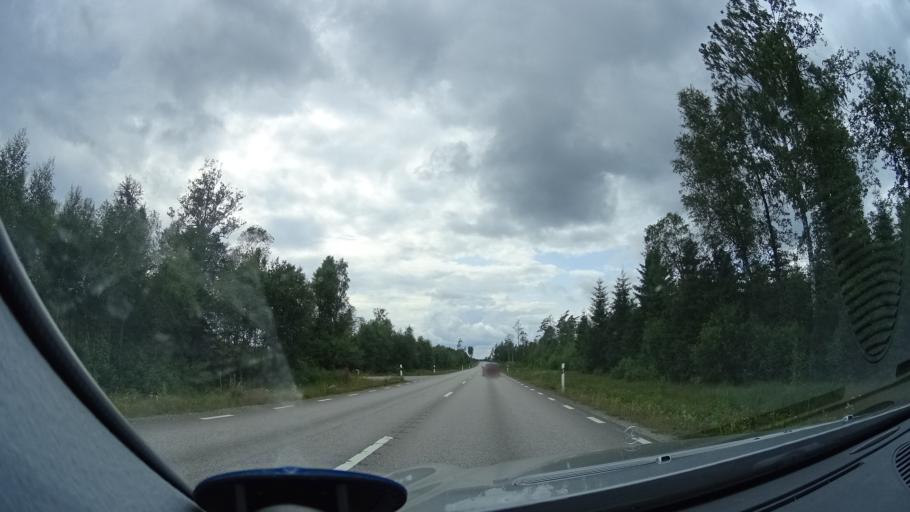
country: SE
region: Kronoberg
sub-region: Tingsryds Kommun
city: Tingsryd
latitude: 56.5101
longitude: 15.0160
